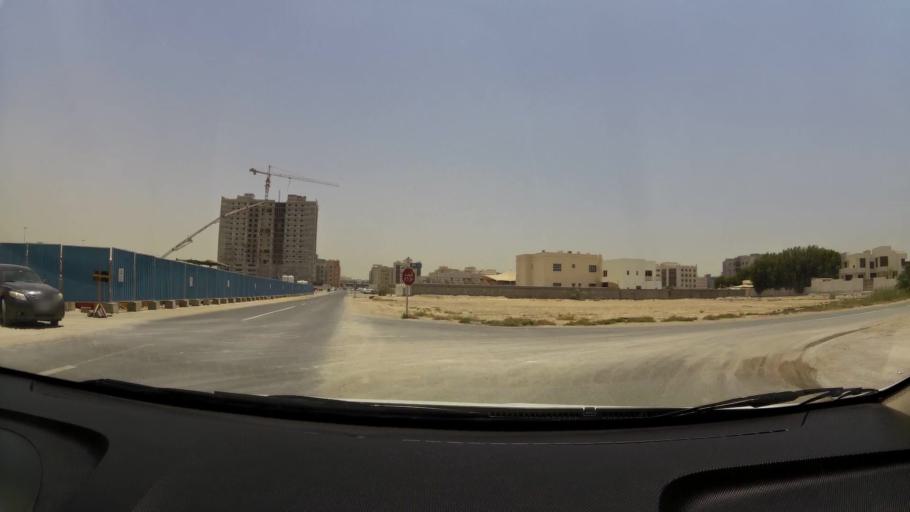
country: AE
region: Ajman
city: Ajman
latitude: 25.4067
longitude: 55.5062
